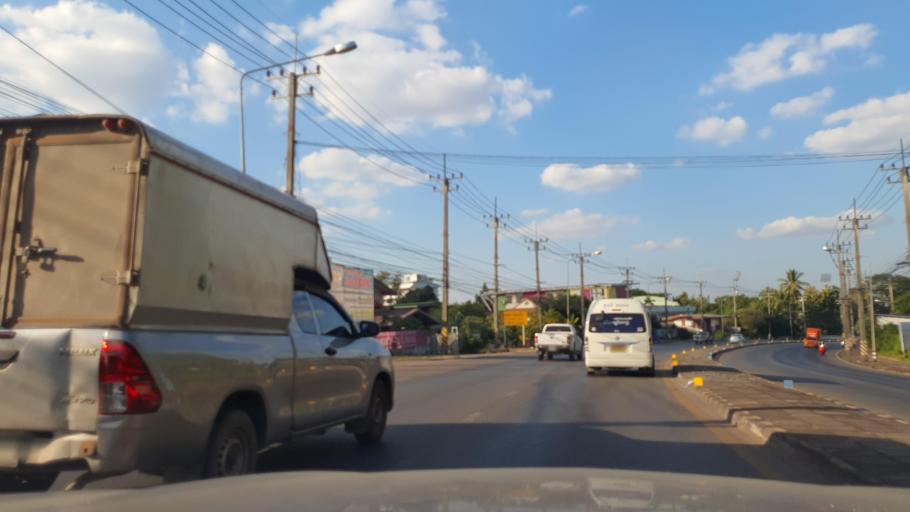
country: TH
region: Sakon Nakhon
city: Sakon Nakhon
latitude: 17.1860
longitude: 104.0930
